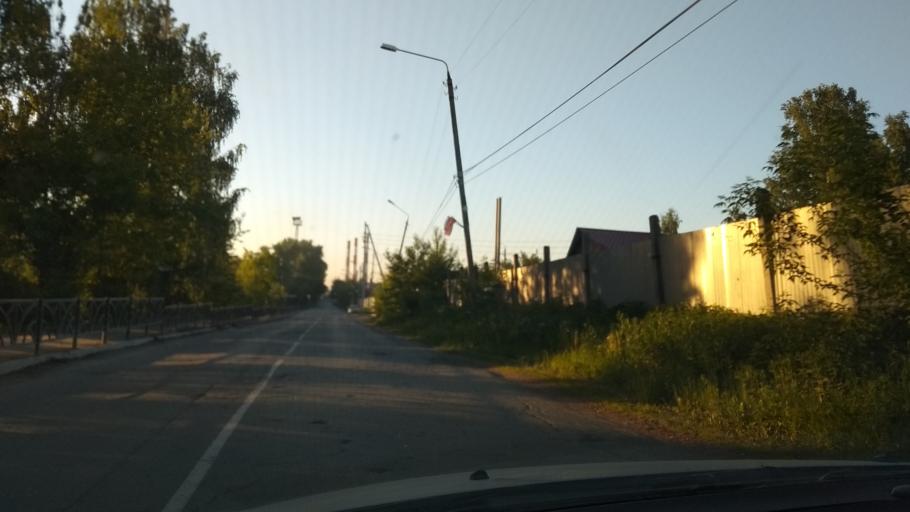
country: RU
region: Sverdlovsk
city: Sredneuralsk
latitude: 56.9834
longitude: 60.4598
